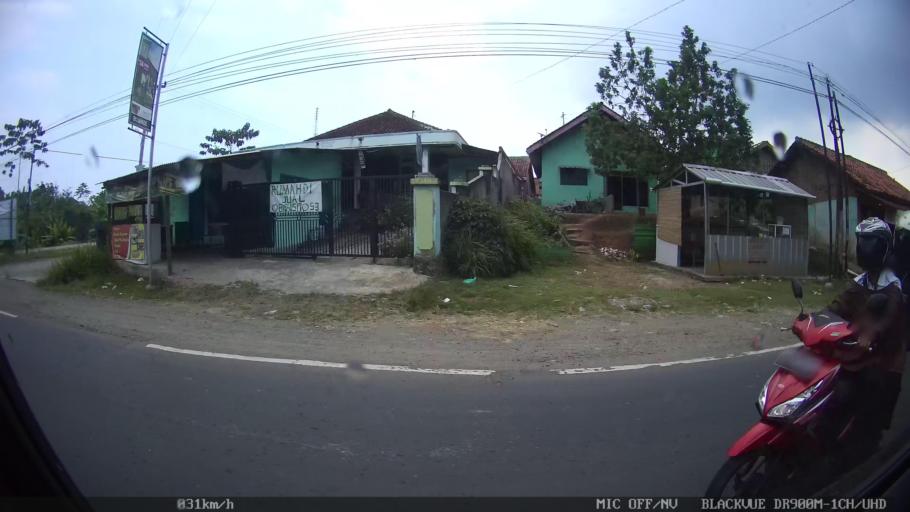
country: ID
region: Lampung
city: Gedongtataan
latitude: -5.3685
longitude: 105.1375
